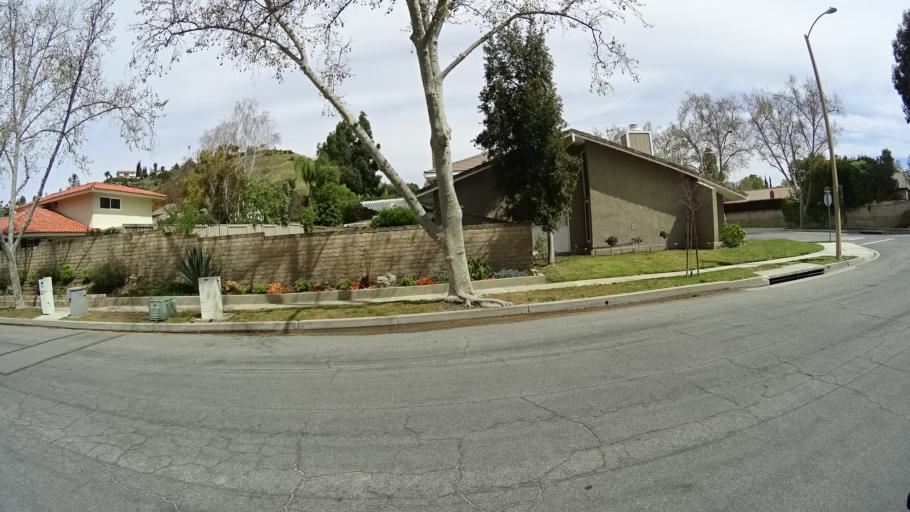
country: US
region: California
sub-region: Ventura County
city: Thousand Oaks
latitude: 34.1478
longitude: -118.8440
